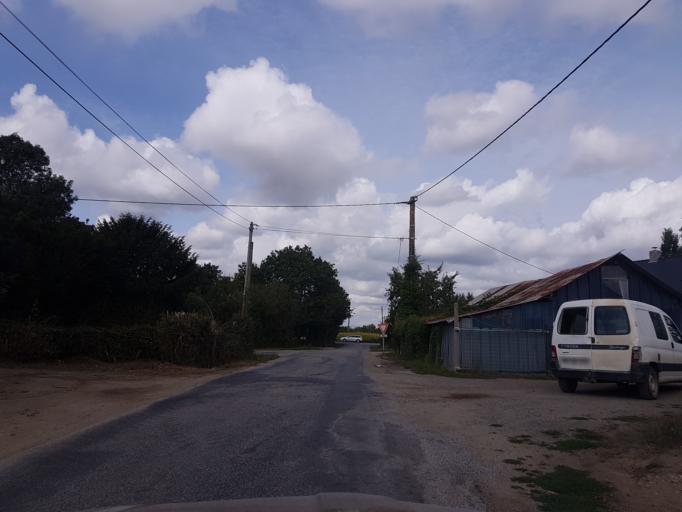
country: FR
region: Pays de la Loire
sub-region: Departement de la Loire-Atlantique
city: Petit-Mars
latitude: 47.4115
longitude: -1.4390
